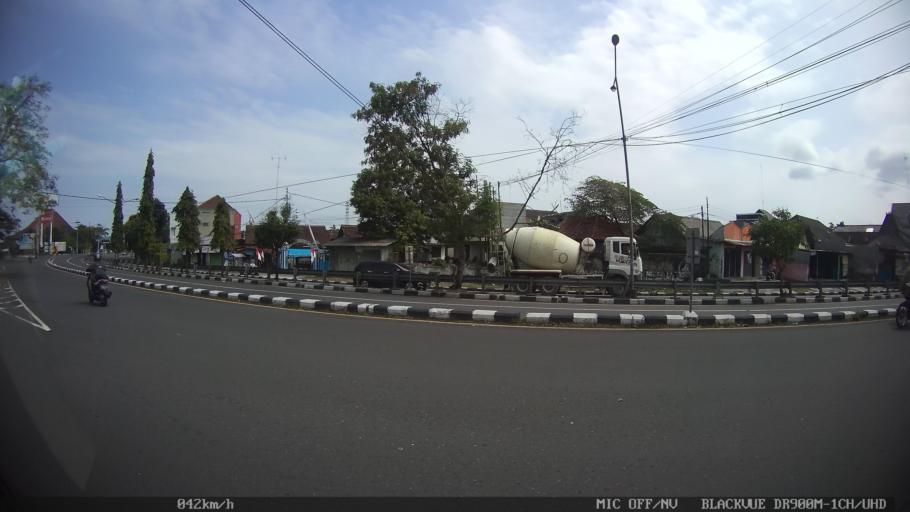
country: ID
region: Daerah Istimewa Yogyakarta
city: Depok
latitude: -7.7669
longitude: 110.4301
